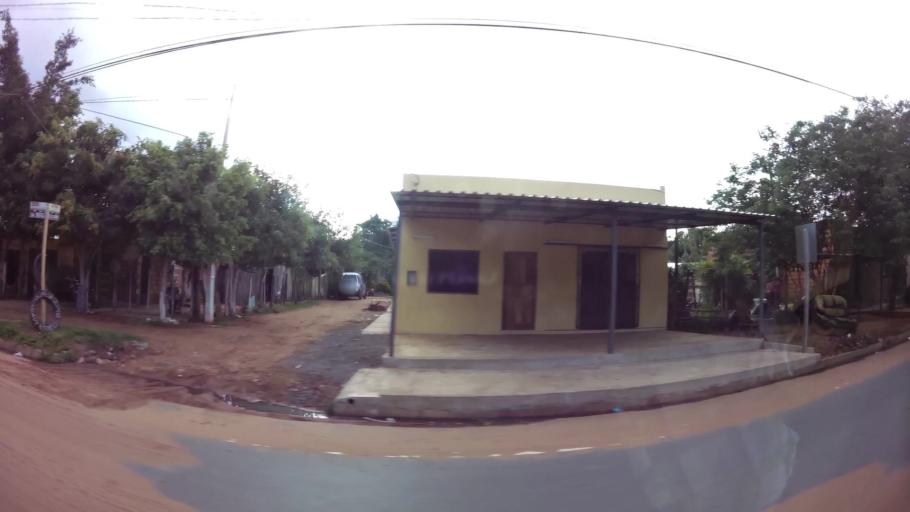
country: PY
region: Central
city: Nemby
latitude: -25.3690
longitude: -57.5416
